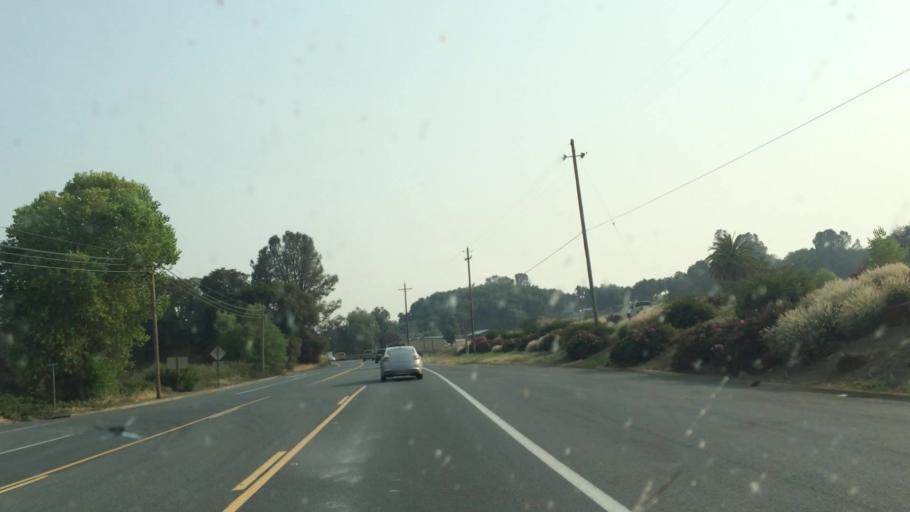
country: US
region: California
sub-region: Amador County
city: Plymouth
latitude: 38.4664
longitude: -120.8555
